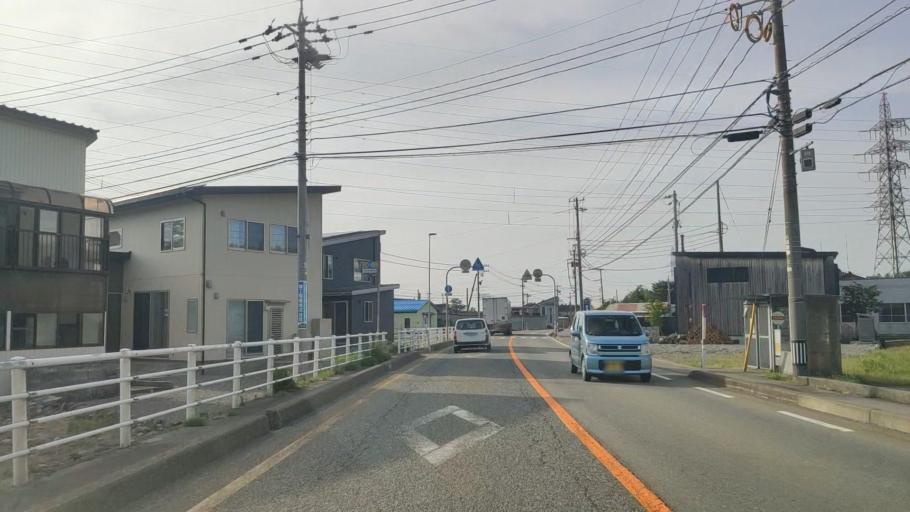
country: JP
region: Toyama
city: Yatsuomachi-higashikumisaka
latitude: 36.5658
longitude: 137.2114
